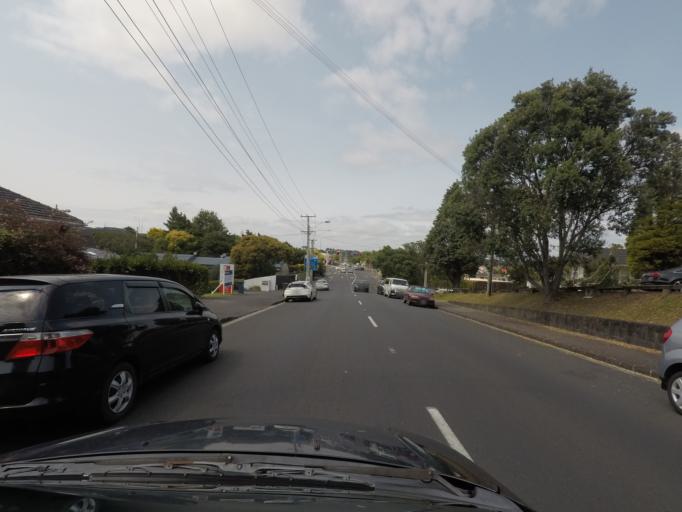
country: NZ
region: Auckland
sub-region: Auckland
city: Rosebank
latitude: -36.9045
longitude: 174.7016
